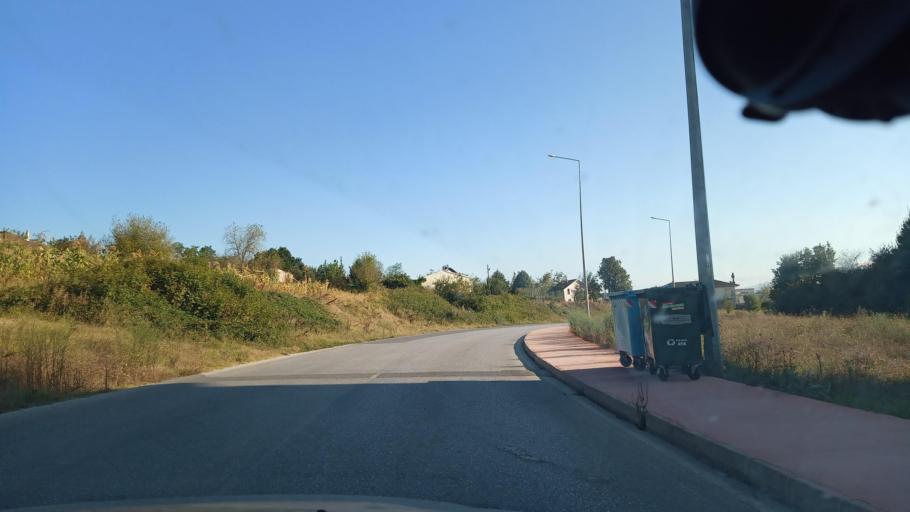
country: TR
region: Sakarya
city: Kazimpasa
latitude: 40.8535
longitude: 30.2799
